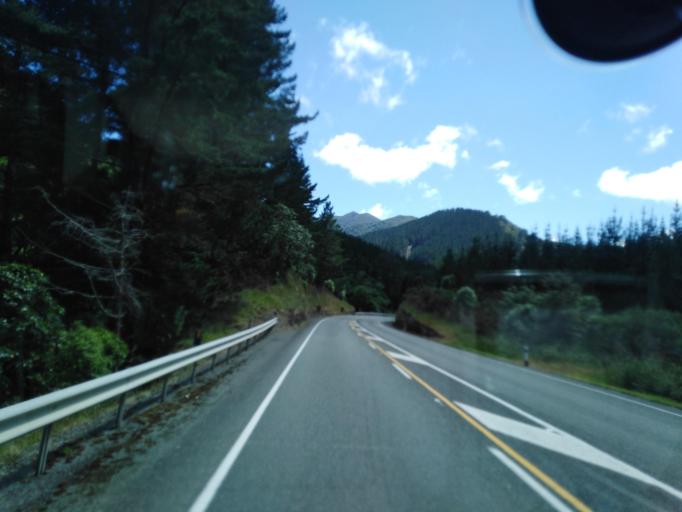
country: NZ
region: Nelson
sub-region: Nelson City
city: Nelson
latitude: -41.1776
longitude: 173.5604
